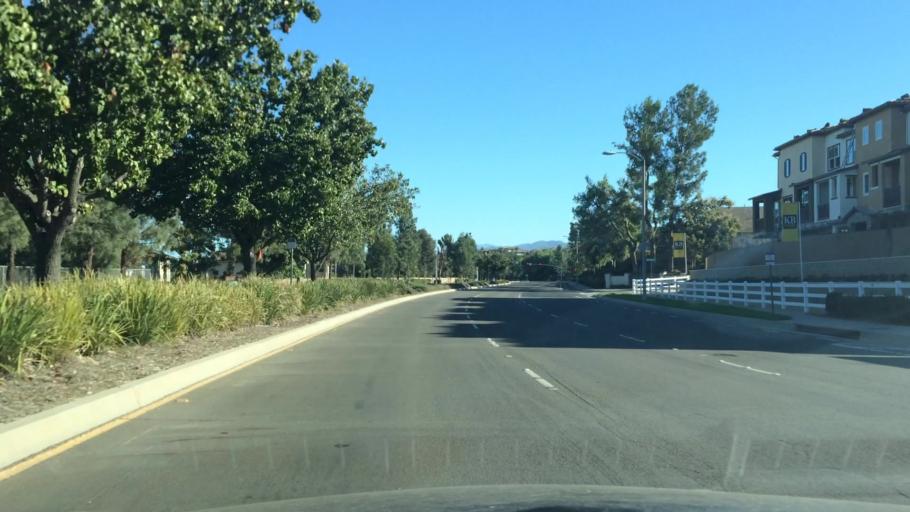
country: US
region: California
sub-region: San Bernardino County
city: Los Serranos
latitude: 33.9601
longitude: -117.6914
